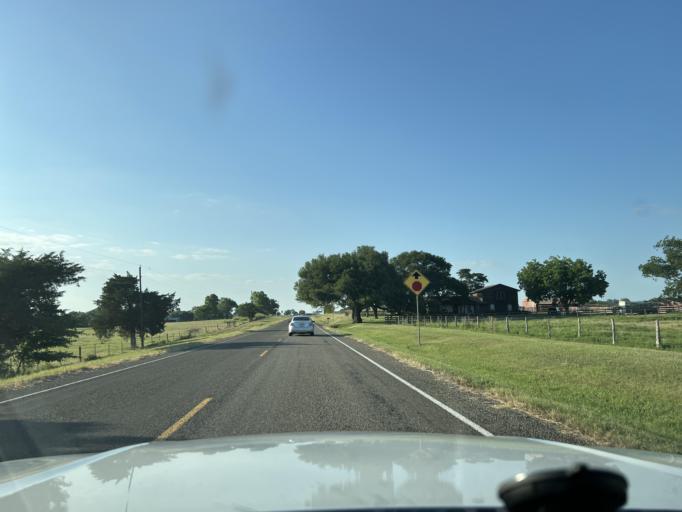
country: US
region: Texas
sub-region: Washington County
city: Brenham
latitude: 30.2262
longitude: -96.3916
